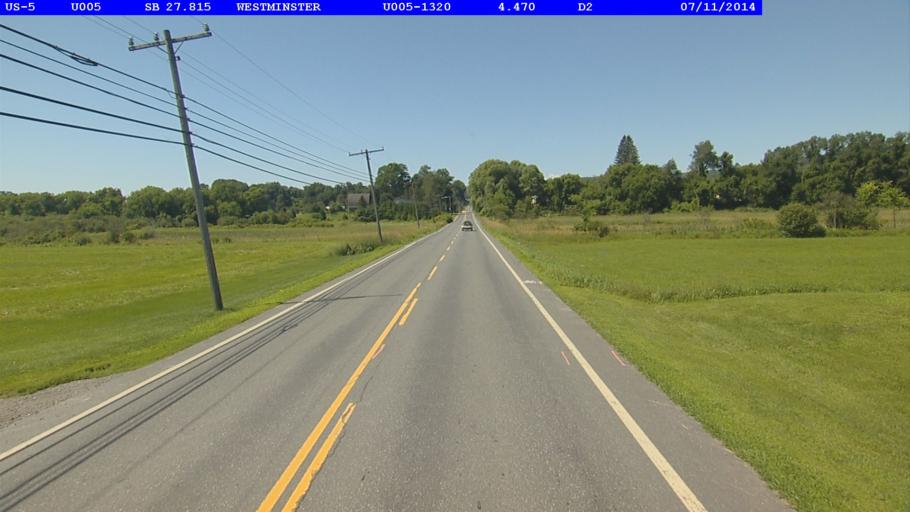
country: US
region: Vermont
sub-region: Windham County
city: Bellows Falls
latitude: 43.0779
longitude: -72.4474
